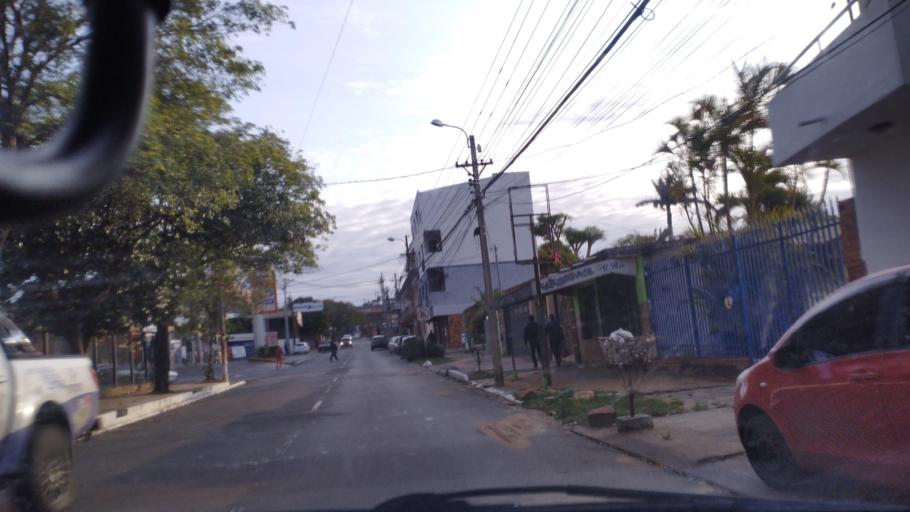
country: PY
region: Central
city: Fernando de la Mora
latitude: -25.3197
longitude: -57.5513
